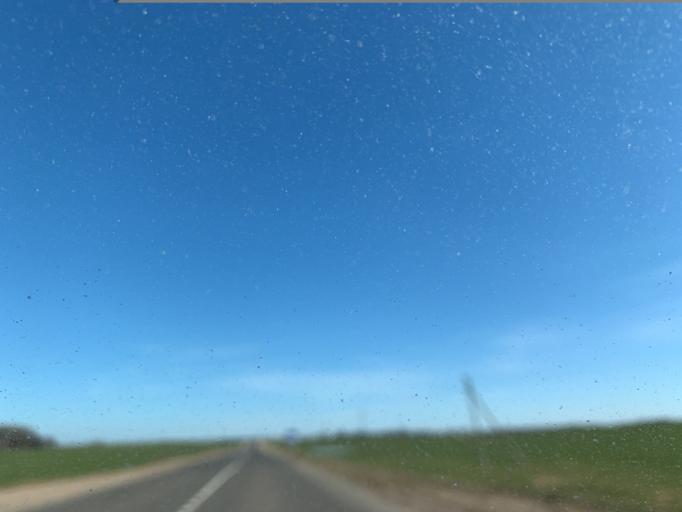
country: BY
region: Minsk
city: Nyasvizh
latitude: 53.2201
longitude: 26.7040
